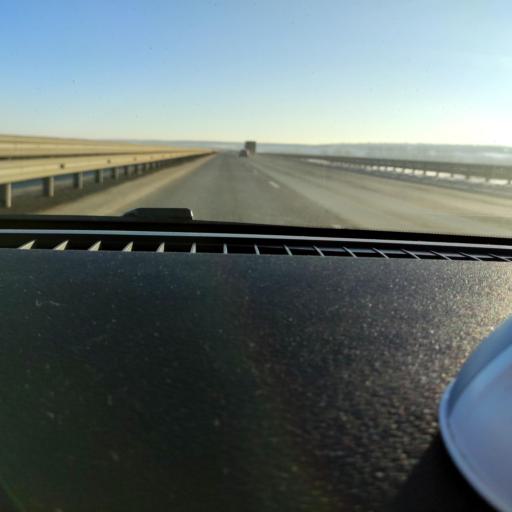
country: RU
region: Samara
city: Smyshlyayevka
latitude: 53.1568
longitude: 50.3384
